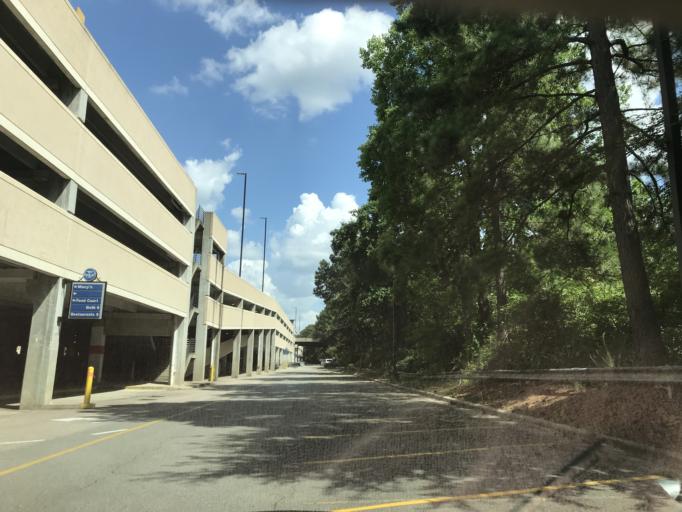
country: US
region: North Carolina
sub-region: Wake County
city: West Raleigh
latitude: 35.8408
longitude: -78.6829
